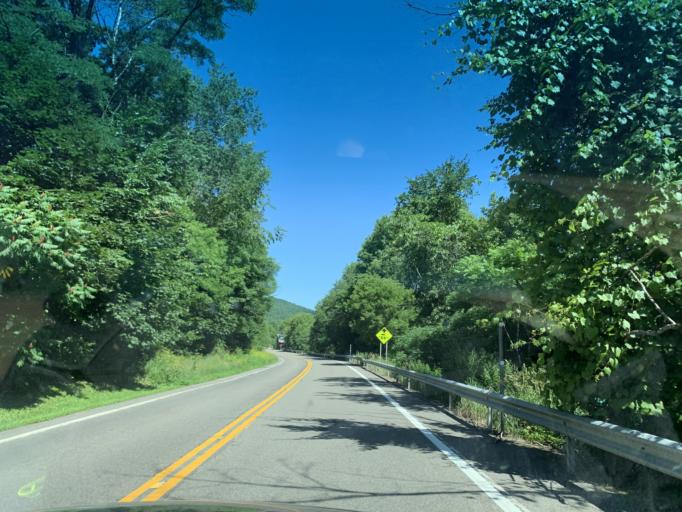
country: US
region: New York
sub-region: Chenango County
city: Norwich
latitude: 42.4988
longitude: -75.4006
